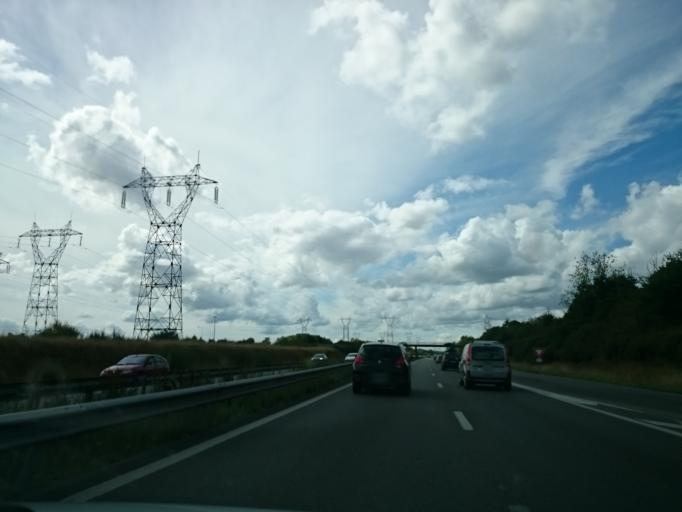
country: FR
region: Pays de la Loire
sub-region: Departement de la Loire-Atlantique
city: Reze
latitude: 47.1602
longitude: -1.5524
